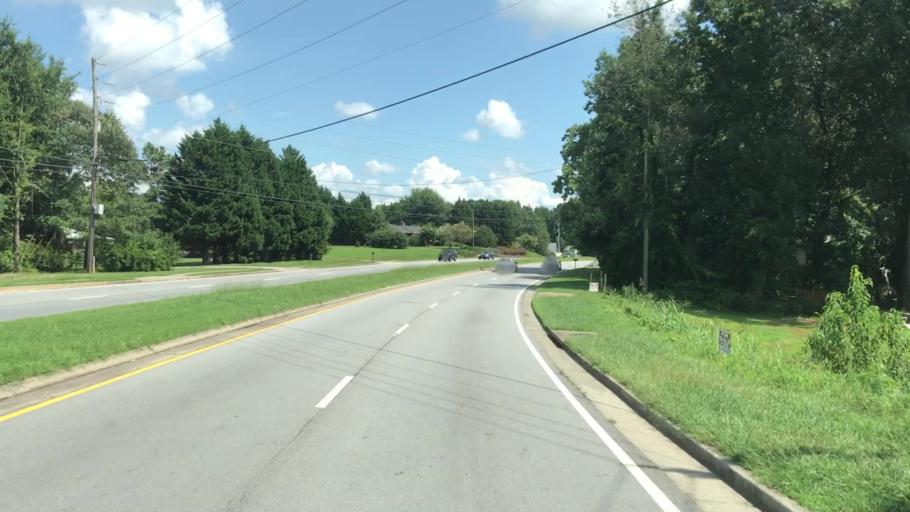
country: US
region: Georgia
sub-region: Gwinnett County
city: Suwanee
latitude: 33.9983
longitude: -84.0367
